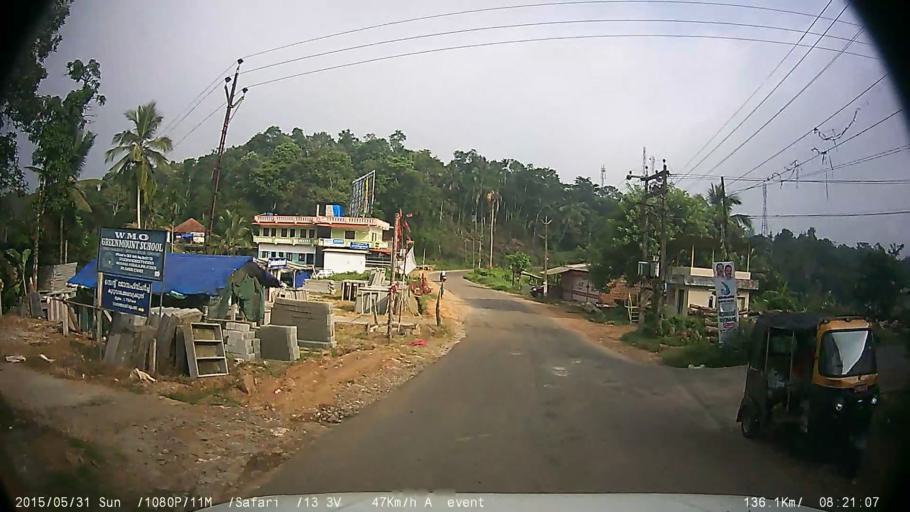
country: IN
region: Kerala
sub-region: Wayanad
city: Kalpetta
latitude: 11.6754
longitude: 75.9782
